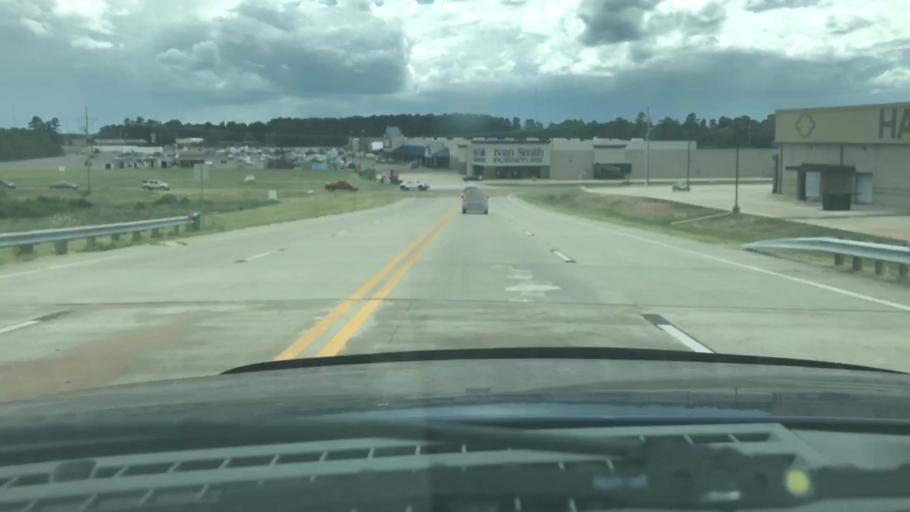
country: US
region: Texas
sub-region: Bowie County
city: Wake Village
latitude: 33.4510
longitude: -94.0998
